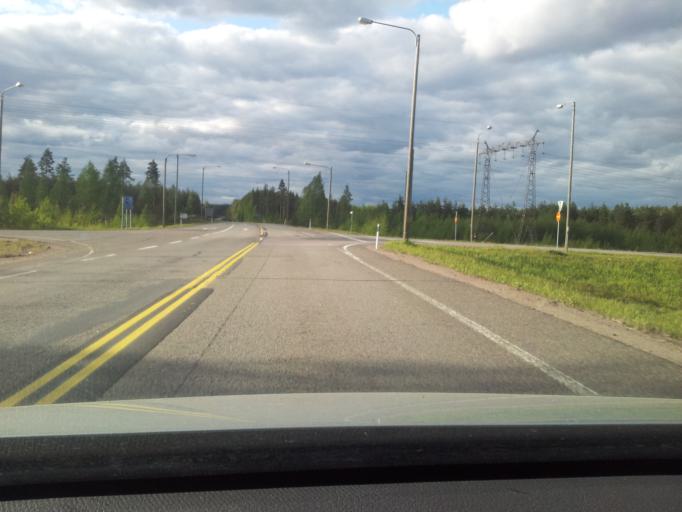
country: FI
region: South Karelia
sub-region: Lappeenranta
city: Luumaeki
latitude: 60.9292
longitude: 27.5839
